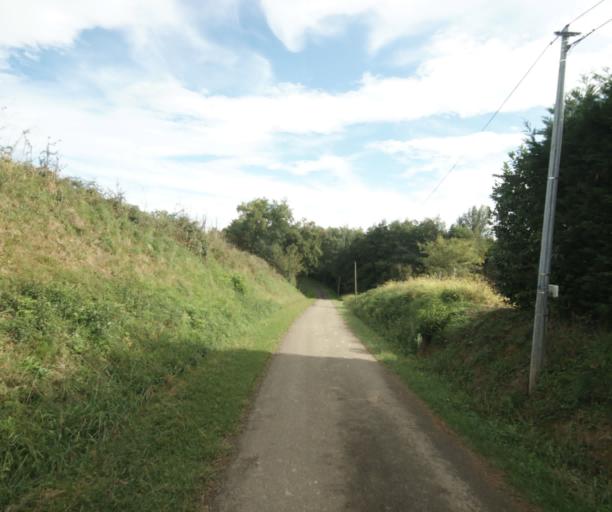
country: FR
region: Midi-Pyrenees
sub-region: Departement du Gers
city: Cazaubon
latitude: 43.8789
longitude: -0.1451
